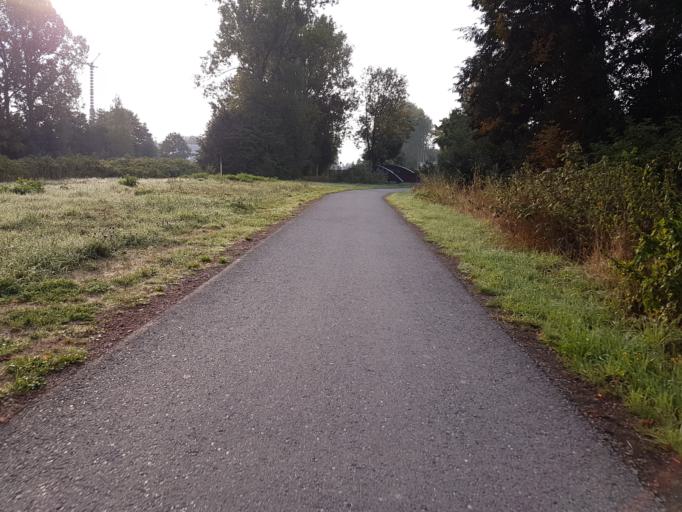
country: DE
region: Saxony
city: Wittgensdorf
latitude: 50.8681
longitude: 12.9036
